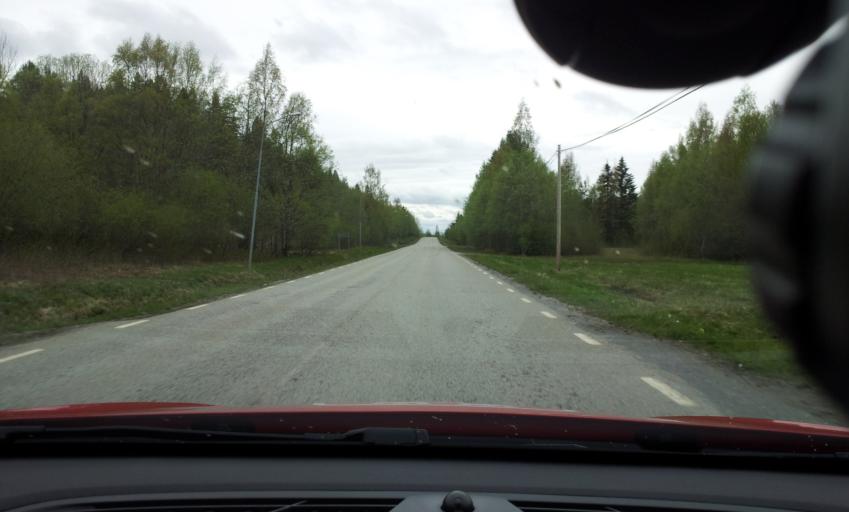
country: SE
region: Jaemtland
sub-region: Bergs Kommun
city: Hoverberg
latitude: 62.7679
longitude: 14.5487
